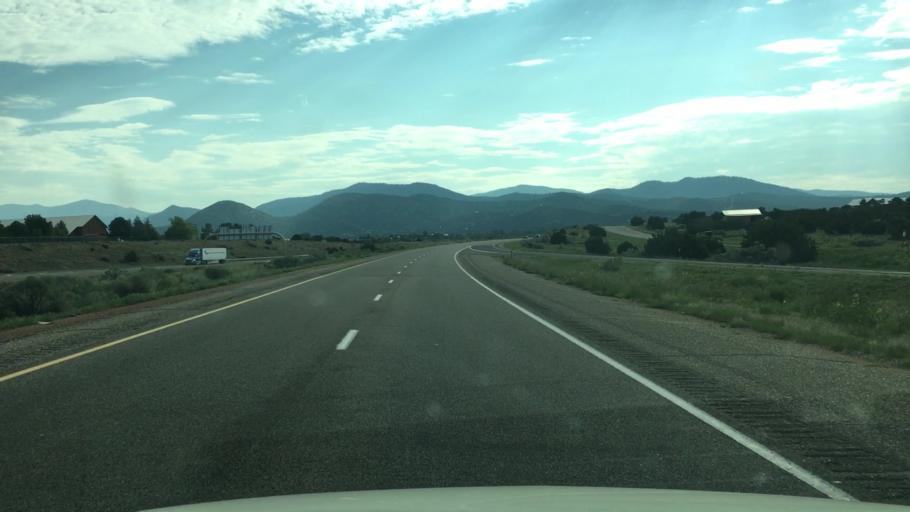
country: US
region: New Mexico
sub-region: Santa Fe County
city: Santa Fe
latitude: 35.6355
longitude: -105.9529
